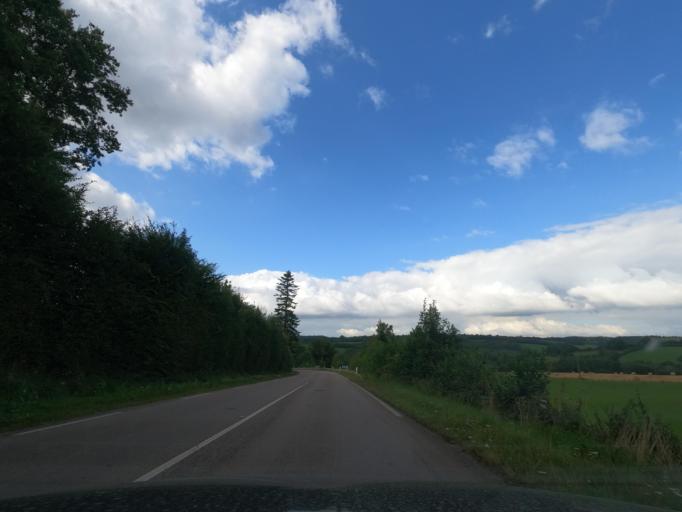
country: FR
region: Lower Normandy
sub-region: Departement de l'Orne
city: Gace
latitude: 48.8041
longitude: 0.3109
